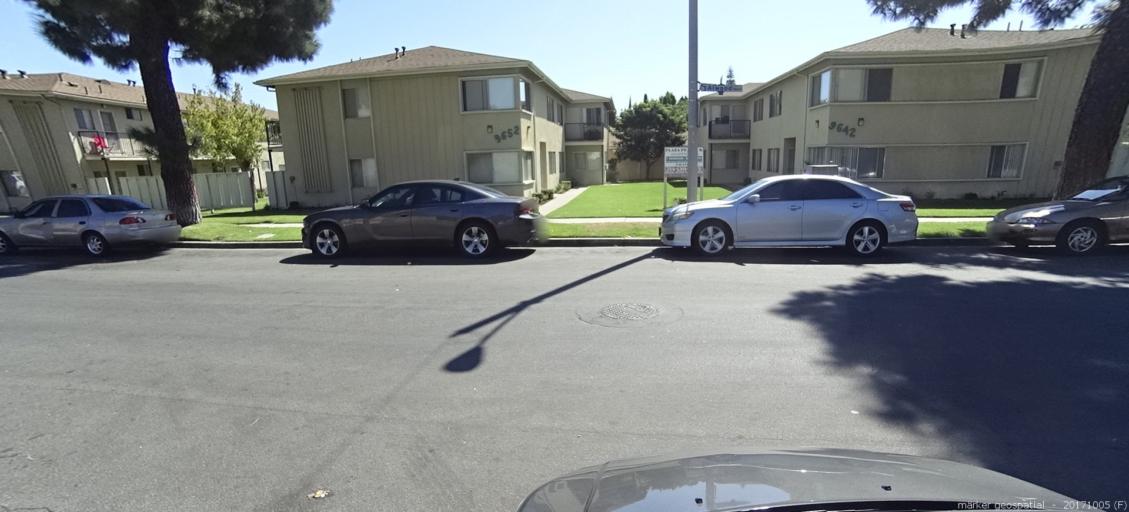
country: US
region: California
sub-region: Orange County
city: Garden Grove
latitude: 33.7873
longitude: -117.9647
